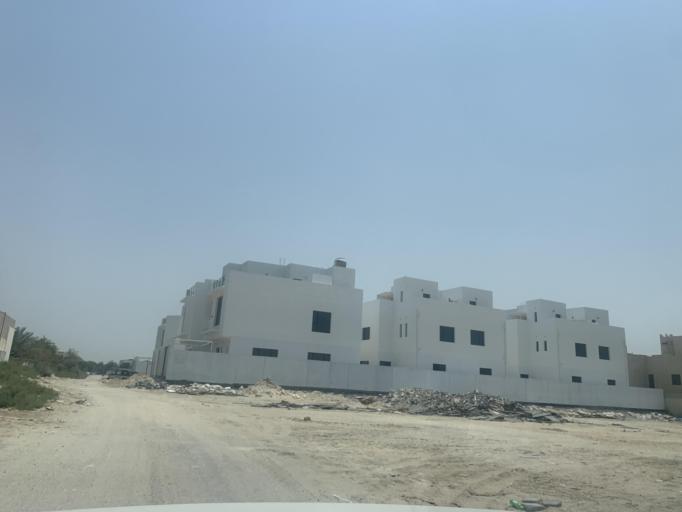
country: BH
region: Central Governorate
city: Madinat Hamad
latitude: 26.1468
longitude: 50.4601
